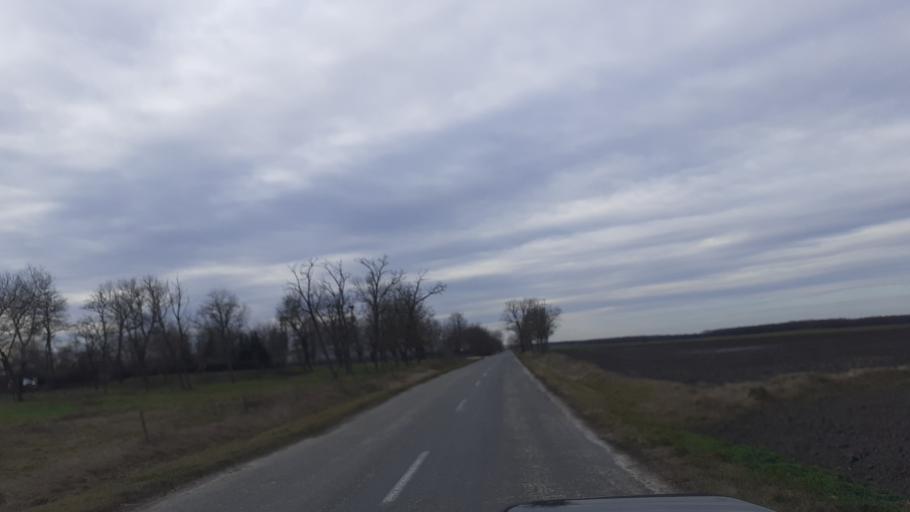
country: HU
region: Fejer
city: Sarbogard
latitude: 46.9078
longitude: 18.5901
